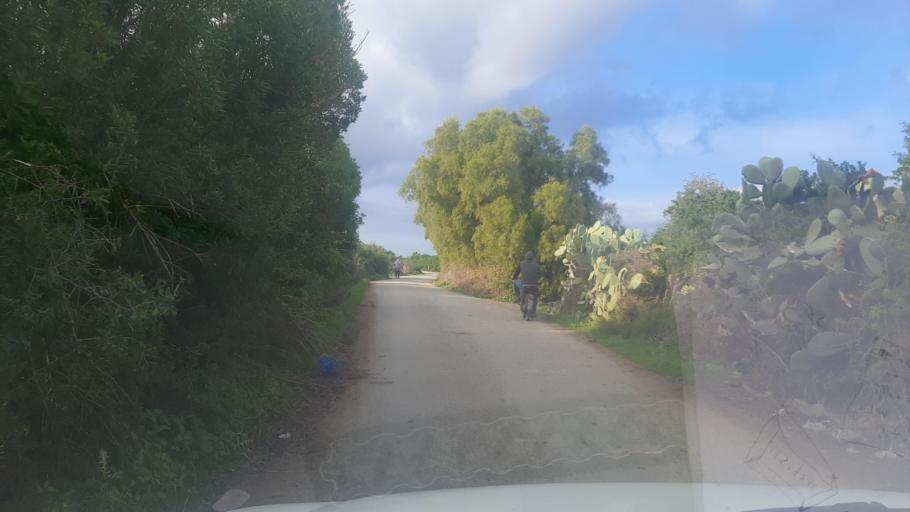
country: TN
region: Nabul
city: Manzil Bu Zalafah
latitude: 36.7123
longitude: 10.4997
